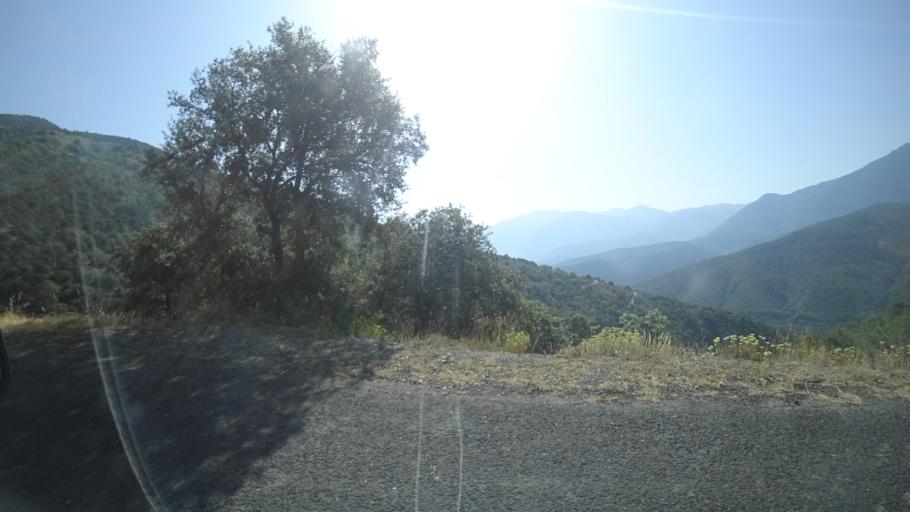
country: FR
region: Languedoc-Roussillon
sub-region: Departement des Pyrenees-Orientales
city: Vernet-les-Bains
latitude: 42.5699
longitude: 2.2984
